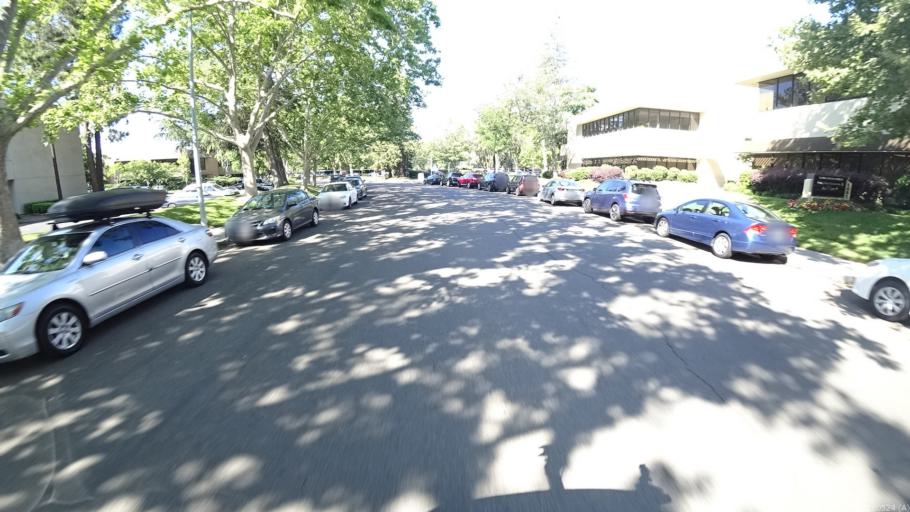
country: US
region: California
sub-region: Sacramento County
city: Sacramento
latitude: 38.5985
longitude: -121.4390
